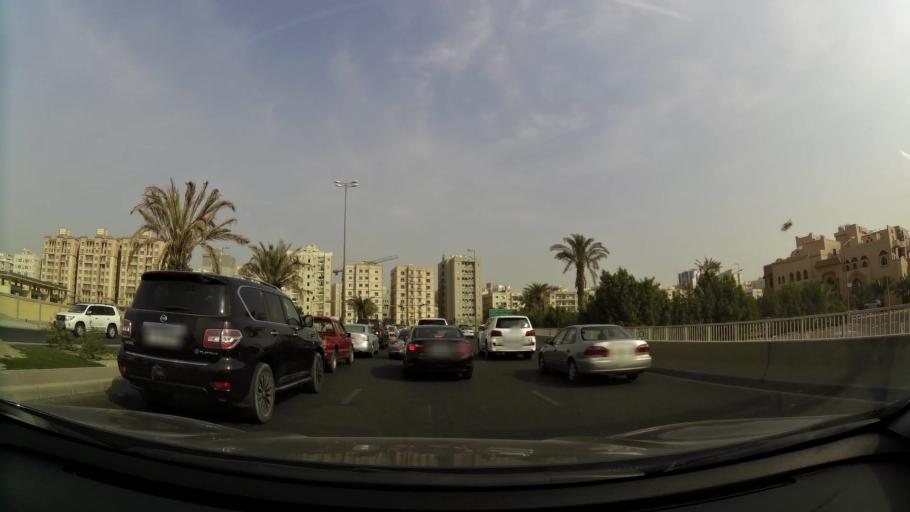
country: KW
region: Al Farwaniyah
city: Al Farwaniyah
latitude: 29.2798
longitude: 47.9481
